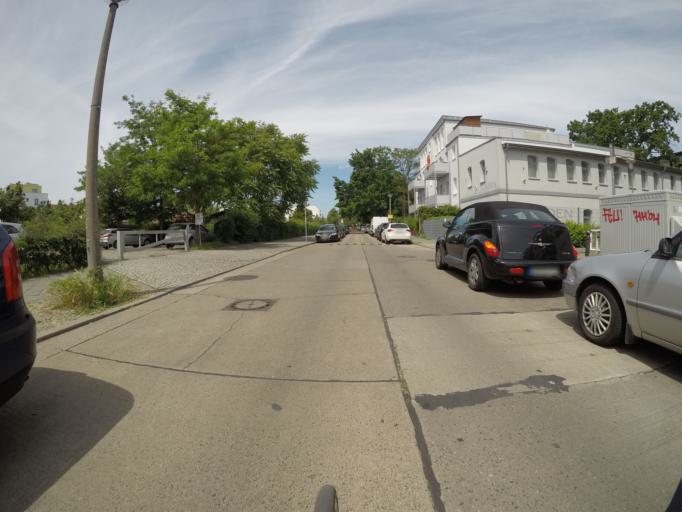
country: DE
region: Berlin
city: Adlershof
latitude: 52.4375
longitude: 13.5574
